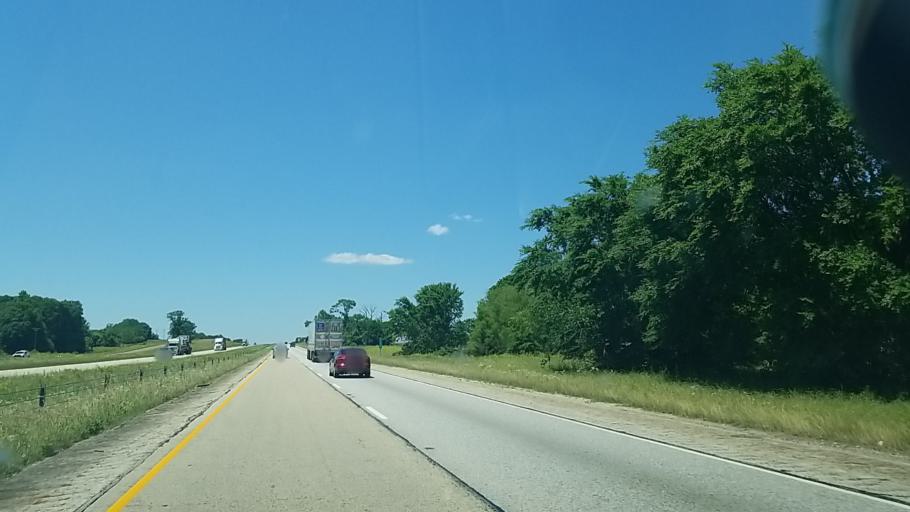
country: US
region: Texas
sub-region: Leon County
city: Centerville
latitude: 31.1566
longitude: -95.9846
